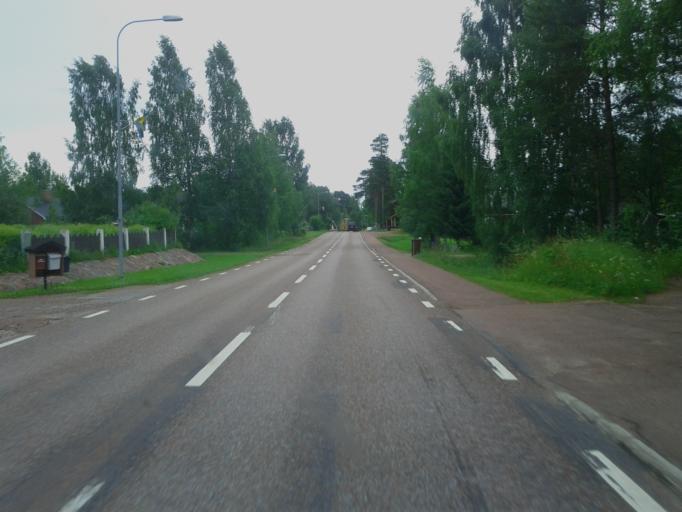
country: NO
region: Hedmark
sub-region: Trysil
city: Innbygda
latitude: 61.6949
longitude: 13.1273
